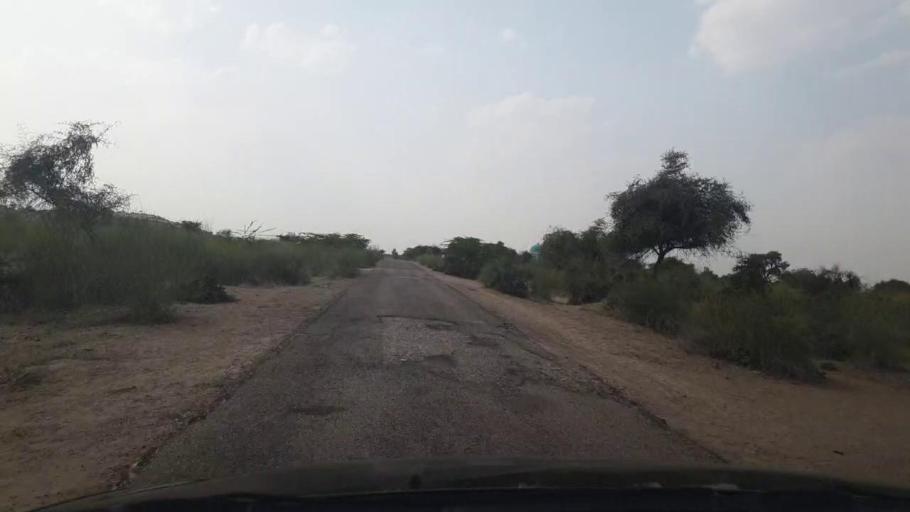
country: PK
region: Sindh
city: Islamkot
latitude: 24.9886
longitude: 70.5725
